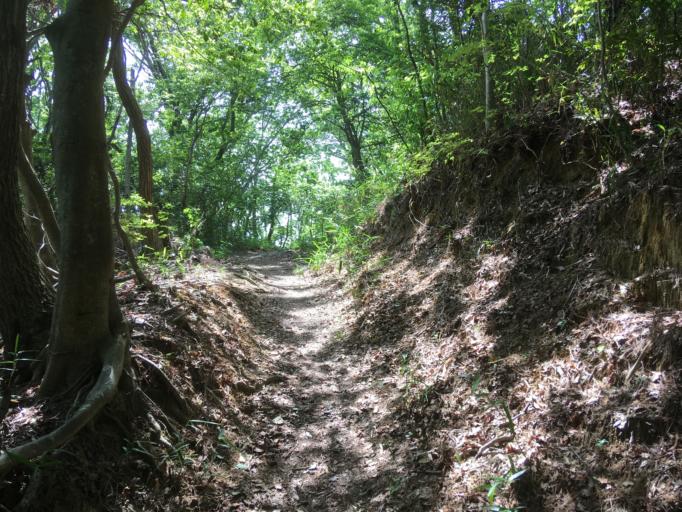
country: JP
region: Nara
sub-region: Ikoma-shi
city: Ikoma
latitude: 34.6529
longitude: 135.6665
